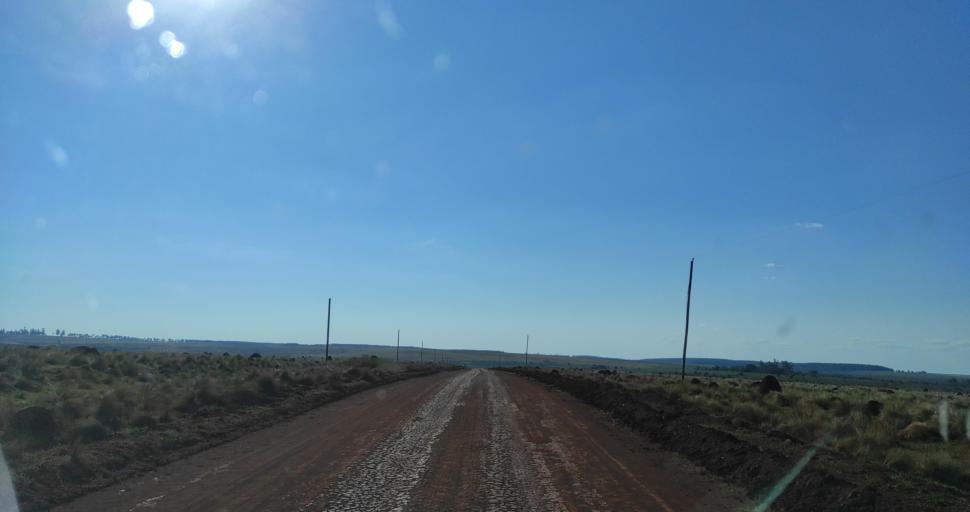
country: PY
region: Itapua
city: San Juan del Parana
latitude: -27.4540
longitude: -56.0610
